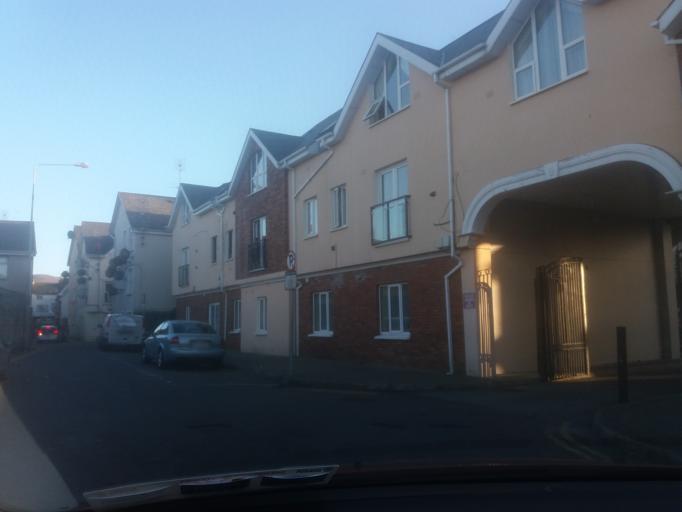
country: IE
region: Munster
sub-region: Ciarrai
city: Cill Airne
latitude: 52.0603
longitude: -9.5119
